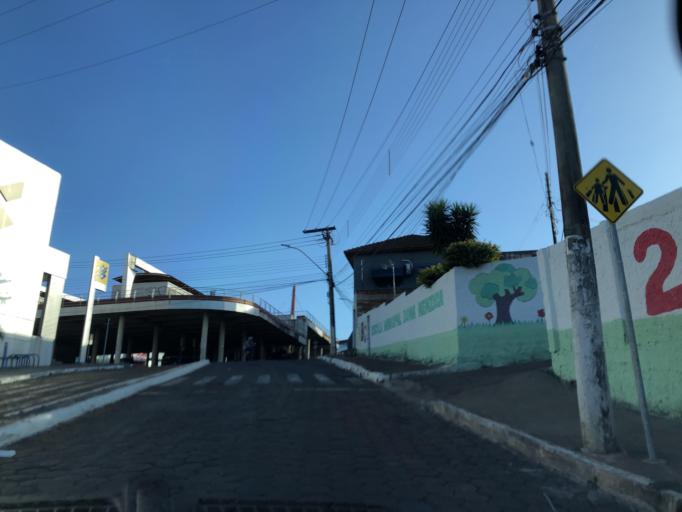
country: BR
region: Goias
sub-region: Luziania
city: Luziania
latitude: -16.2517
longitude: -47.9498
